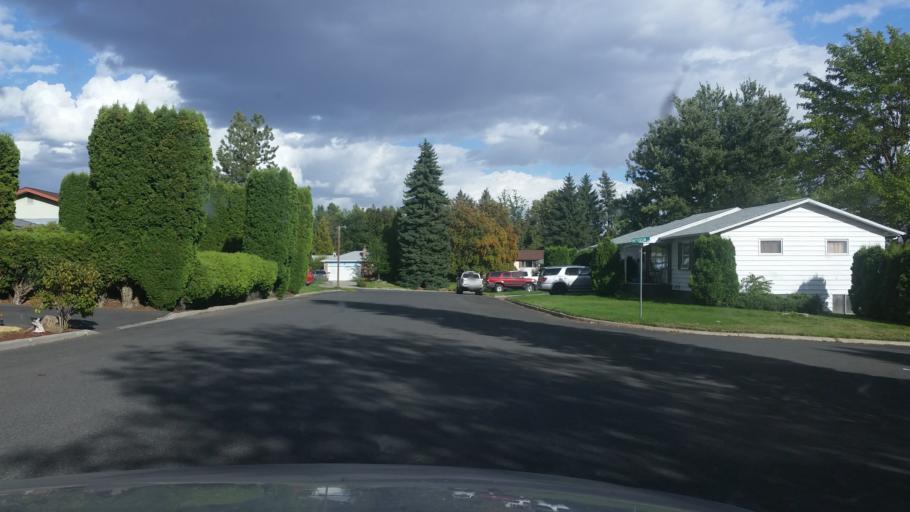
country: US
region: Washington
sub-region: Spokane County
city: Cheney
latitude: 47.4838
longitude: -117.5935
